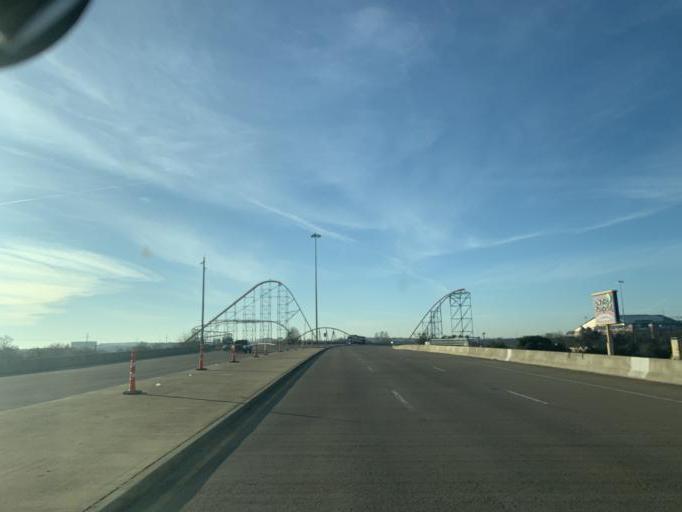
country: US
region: Texas
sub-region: Tarrant County
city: Arlington
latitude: 32.7600
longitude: -97.0760
